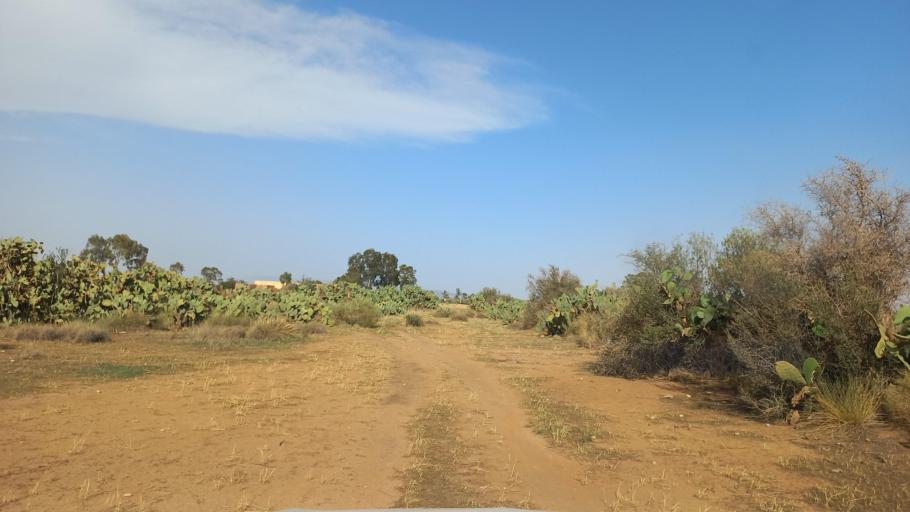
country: TN
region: Al Qasrayn
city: Kasserine
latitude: 35.2243
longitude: 8.9667
